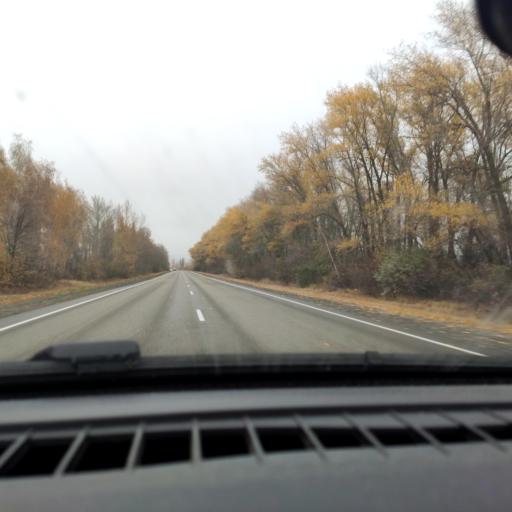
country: RU
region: Voronezj
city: Ostrogozhsk
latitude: 50.9961
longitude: 38.9996
